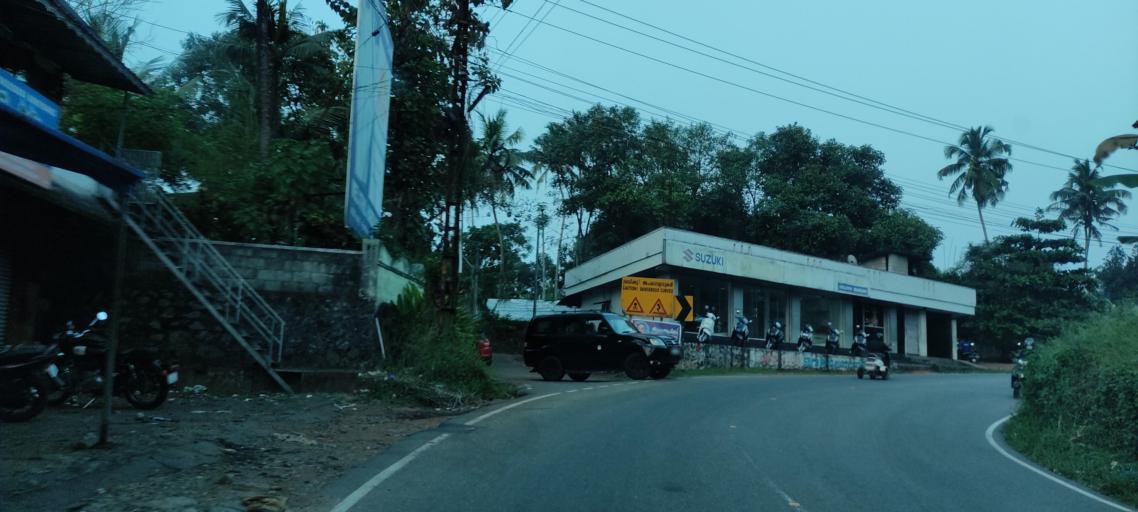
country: IN
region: Kerala
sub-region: Pattanamtitta
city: Adur
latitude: 9.1568
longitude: 76.7414
